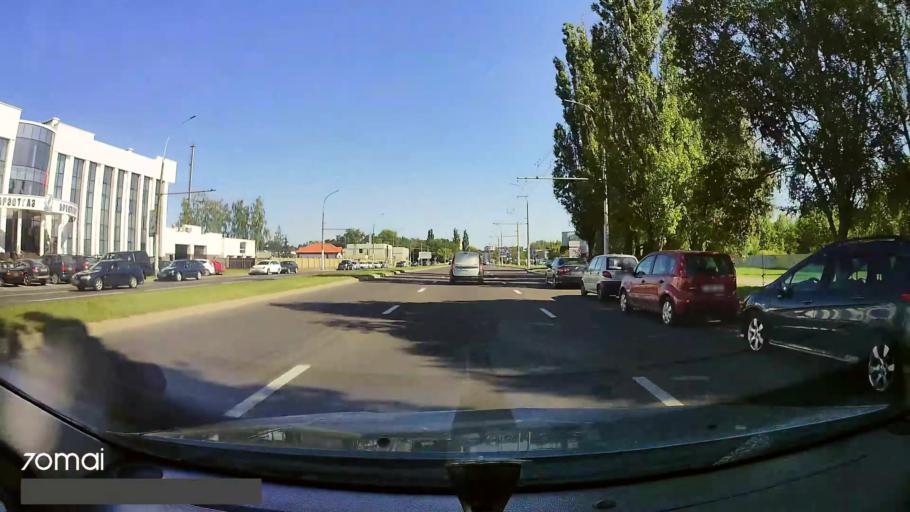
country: BY
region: Brest
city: Brest
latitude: 52.1071
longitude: 23.7435
